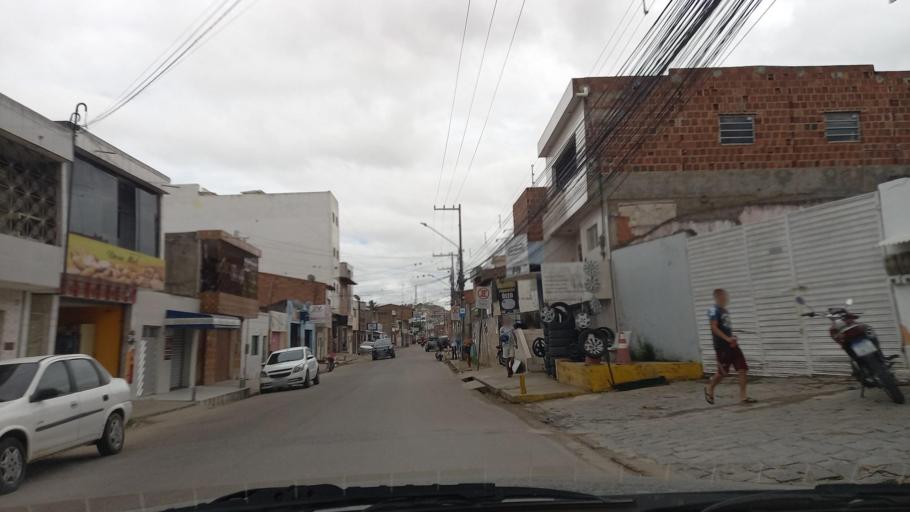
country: BR
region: Pernambuco
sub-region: Caruaru
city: Caruaru
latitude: -8.2827
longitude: -35.9572
